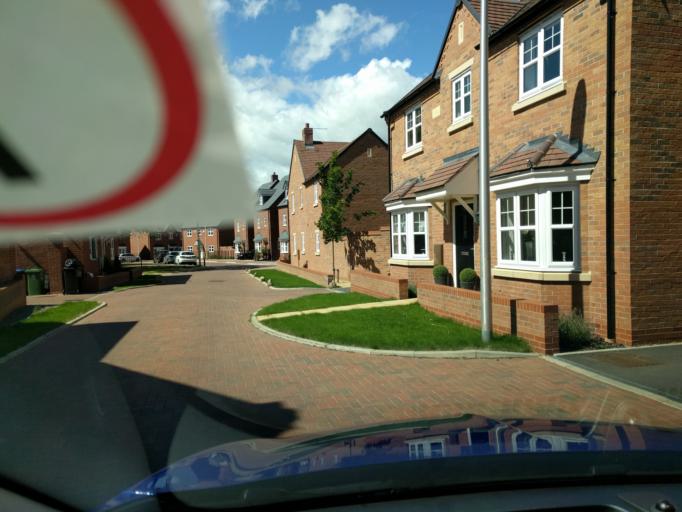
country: GB
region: England
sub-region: Gloucestershire
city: Mickleton
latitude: 52.1176
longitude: -1.7571
